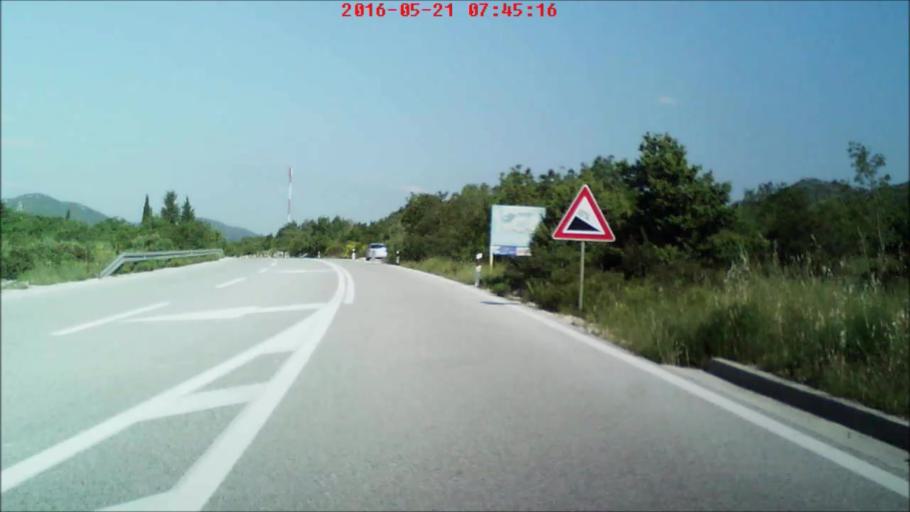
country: HR
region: Dubrovacko-Neretvanska
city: Ston
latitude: 42.8220
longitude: 17.7674
